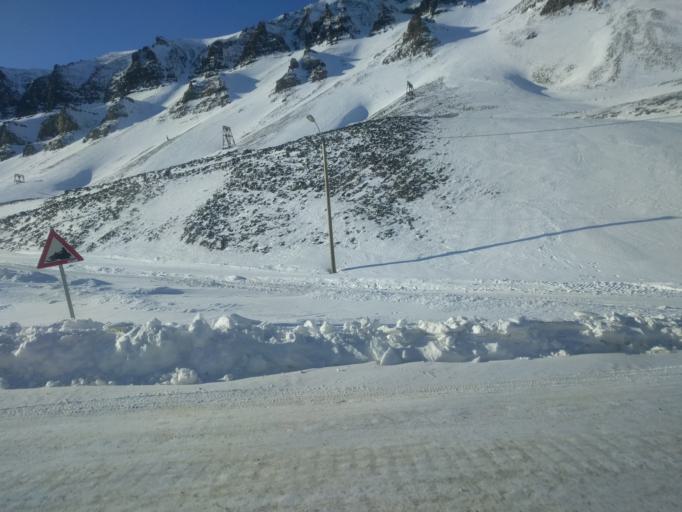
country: SJ
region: Svalbard
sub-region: Spitsbergen
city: Longyearbyen
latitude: 78.2075
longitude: 15.5887
